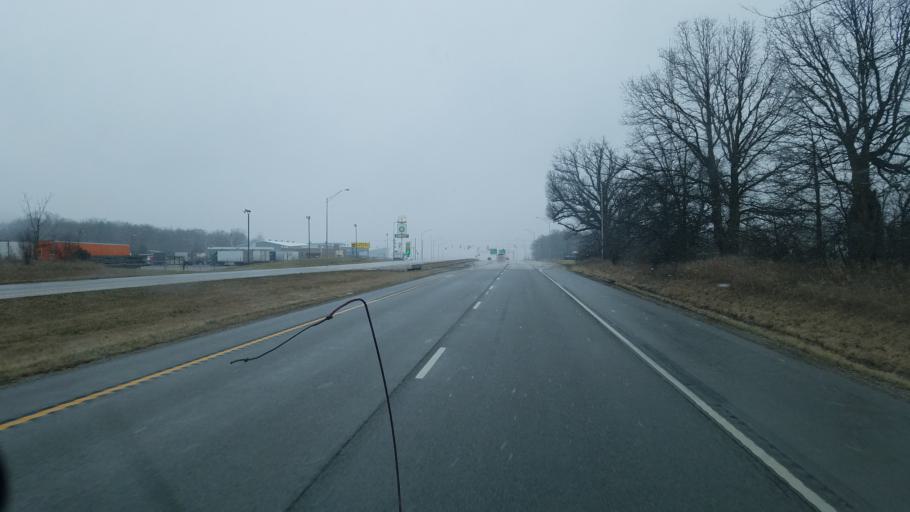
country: US
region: Indiana
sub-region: Miami County
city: Peru
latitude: 40.7816
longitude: -86.1293
